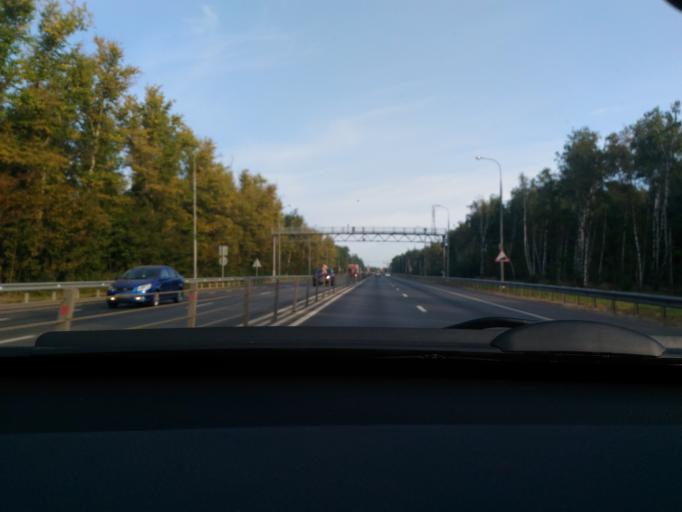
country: RU
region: Moskovskaya
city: Lugovaya
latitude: 56.0610
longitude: 37.5237
